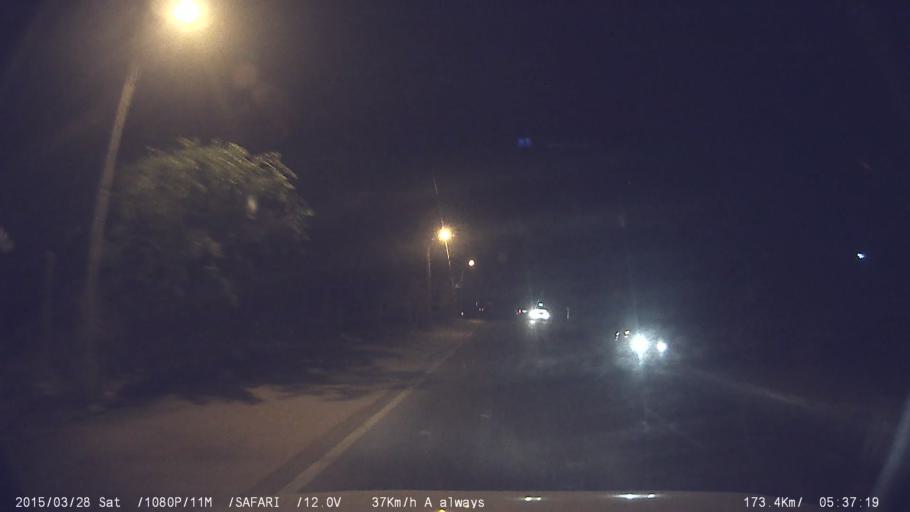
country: IN
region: Karnataka
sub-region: Bangalore Urban
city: Bangalore
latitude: 12.8522
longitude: 77.5884
